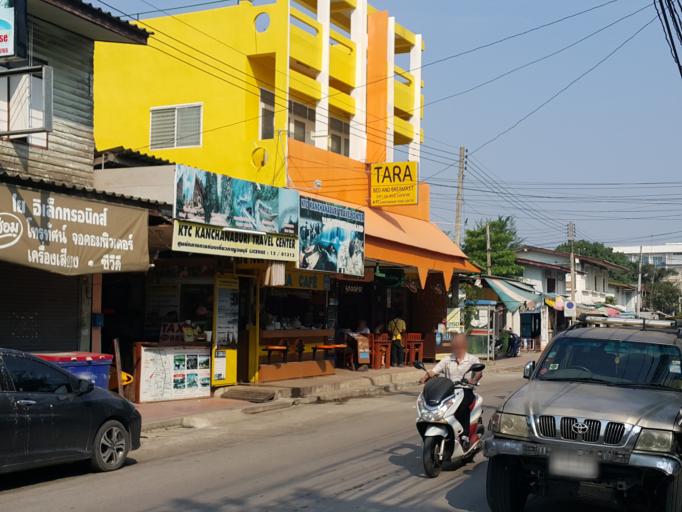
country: TH
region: Kanchanaburi
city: Kanchanaburi
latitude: 14.0346
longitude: 99.5189
